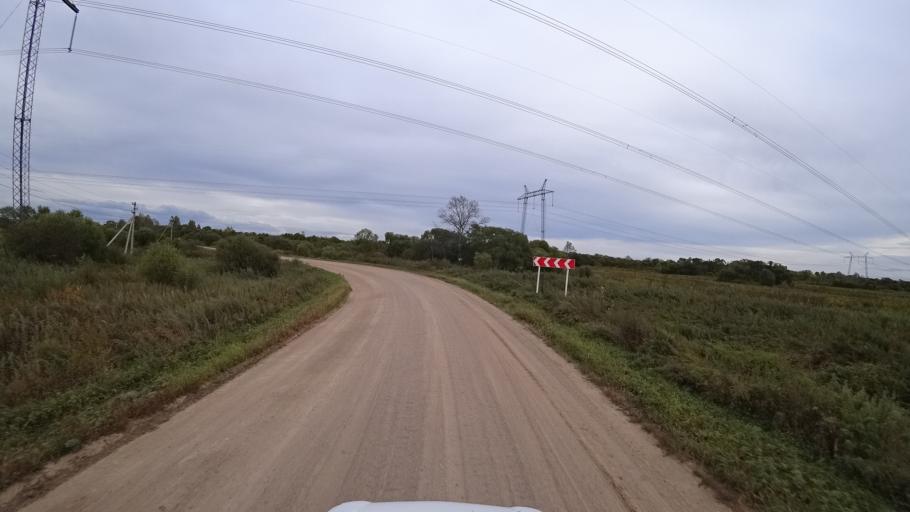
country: RU
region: Amur
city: Arkhara
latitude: 49.4297
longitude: 130.2498
